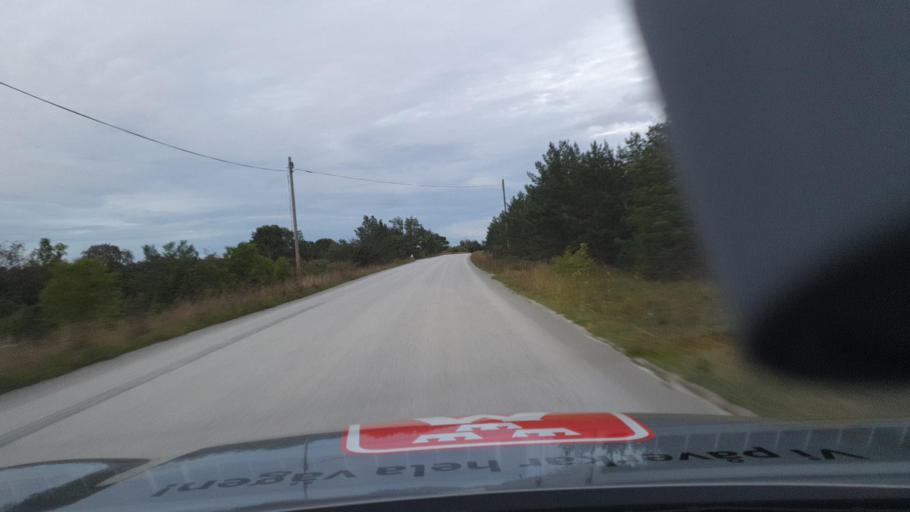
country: SE
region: Gotland
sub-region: Gotland
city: Visby
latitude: 57.6360
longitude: 18.3554
